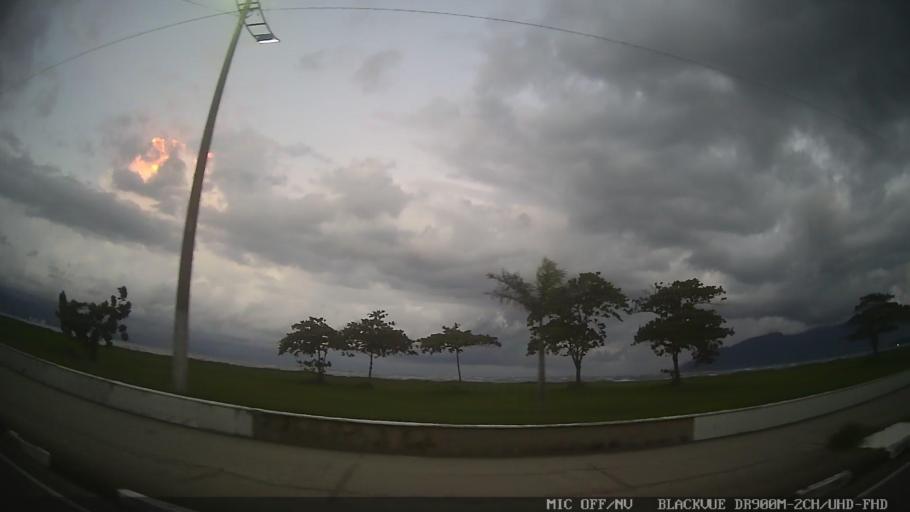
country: BR
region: Sao Paulo
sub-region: Caraguatatuba
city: Caraguatatuba
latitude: -23.6881
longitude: -45.4313
